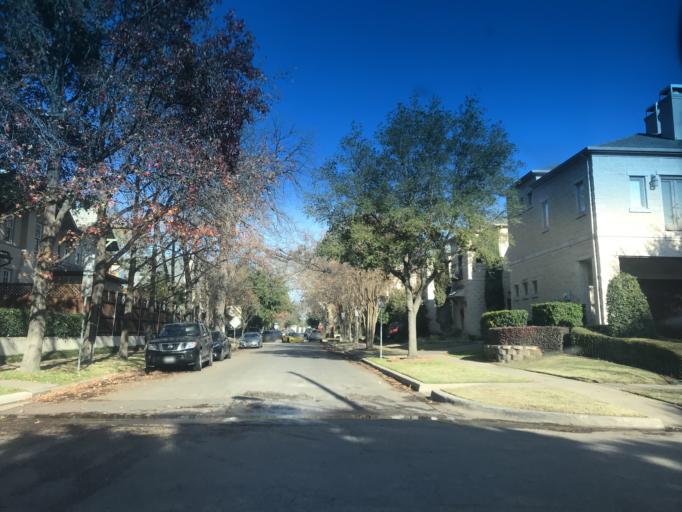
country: US
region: Texas
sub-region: Dallas County
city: Highland Park
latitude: 32.8135
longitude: -96.8059
